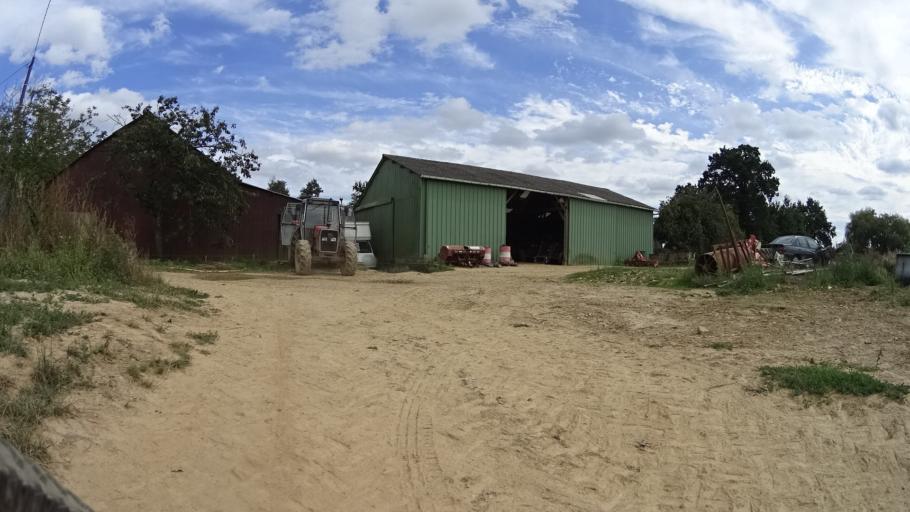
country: FR
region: Brittany
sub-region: Departement d'Ille-et-Vilaine
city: Vignoc
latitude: 48.2350
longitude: -1.7798
